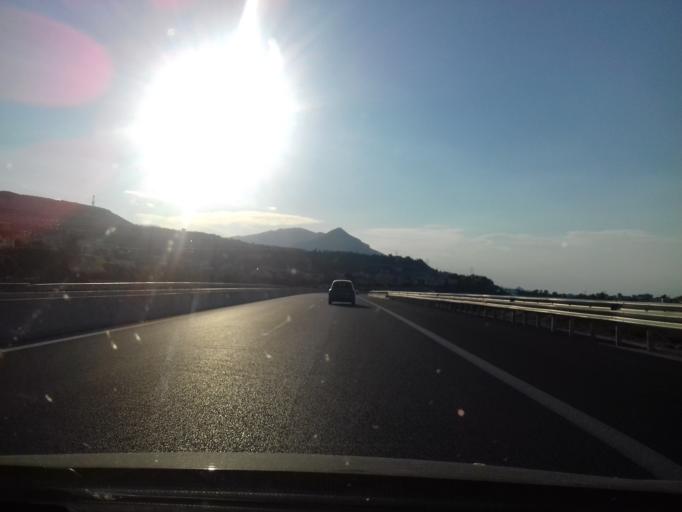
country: GR
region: Peloponnese
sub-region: Nomos Korinthias
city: Xylokastro
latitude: 38.0650
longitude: 22.6506
